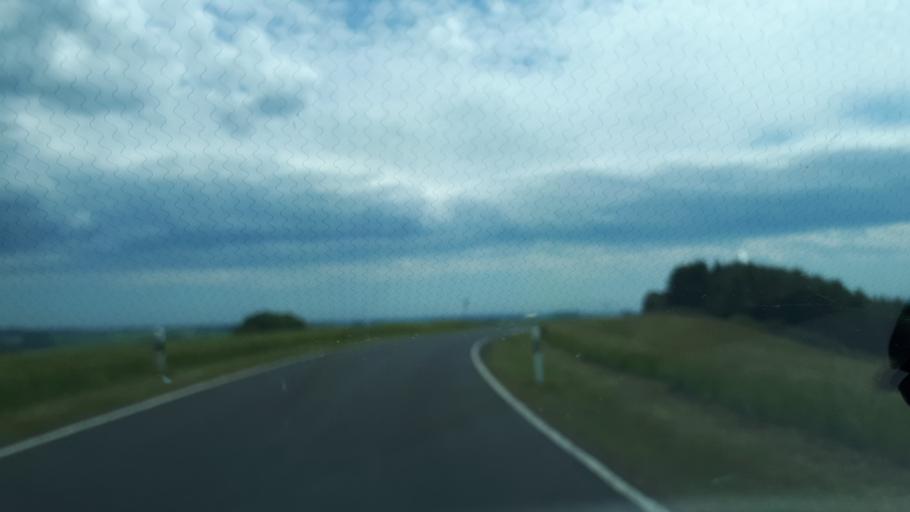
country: DE
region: Rheinland-Pfalz
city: Immerath
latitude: 50.1375
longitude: 6.9573
